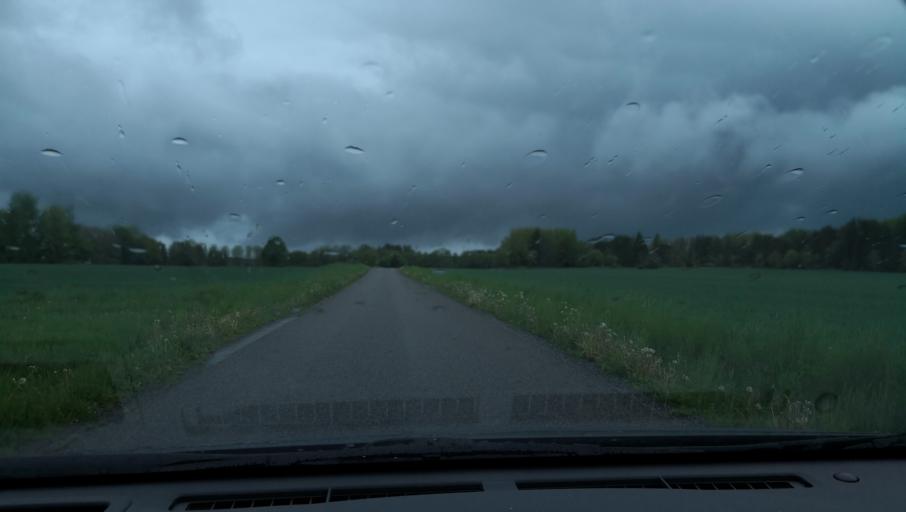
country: SE
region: Uppsala
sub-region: Enkopings Kommun
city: Orsundsbro
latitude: 59.8042
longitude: 17.3781
